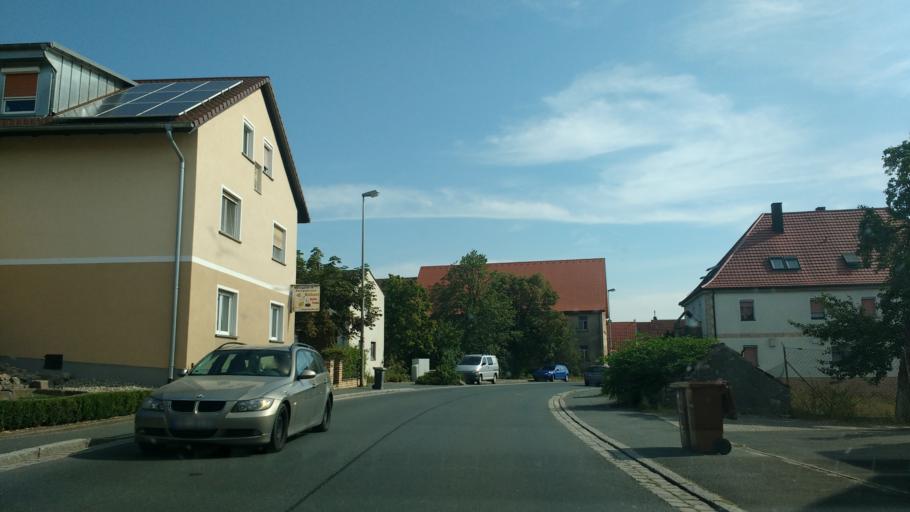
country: DE
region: Bavaria
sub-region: Regierungsbezirk Mittelfranken
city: Grossenseebach
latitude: 49.6312
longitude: 10.8732
